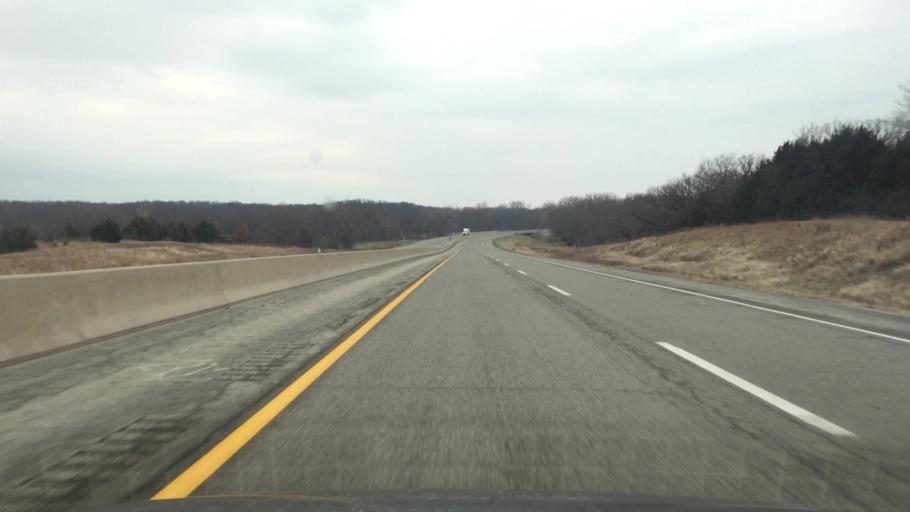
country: US
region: Kansas
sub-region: Shawnee County
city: Auburn
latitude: 38.8972
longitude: -95.8014
